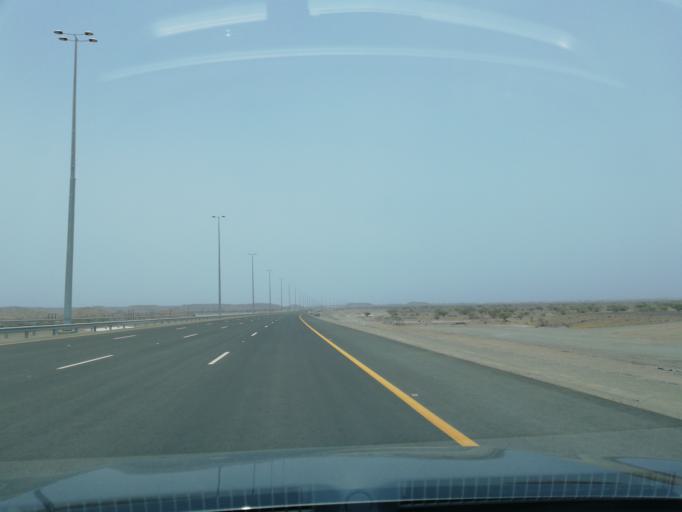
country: OM
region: Al Batinah
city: Al Liwa'
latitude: 24.4764
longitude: 56.5076
